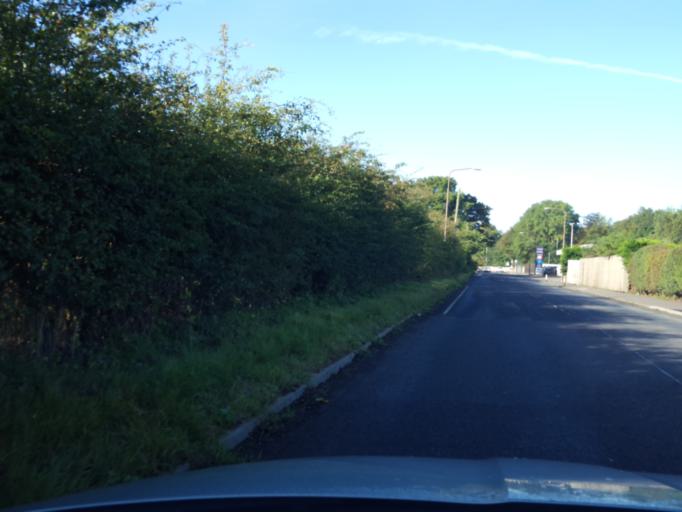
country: GB
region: Scotland
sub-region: West Lothian
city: East Calder
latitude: 55.8978
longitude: -3.4507
